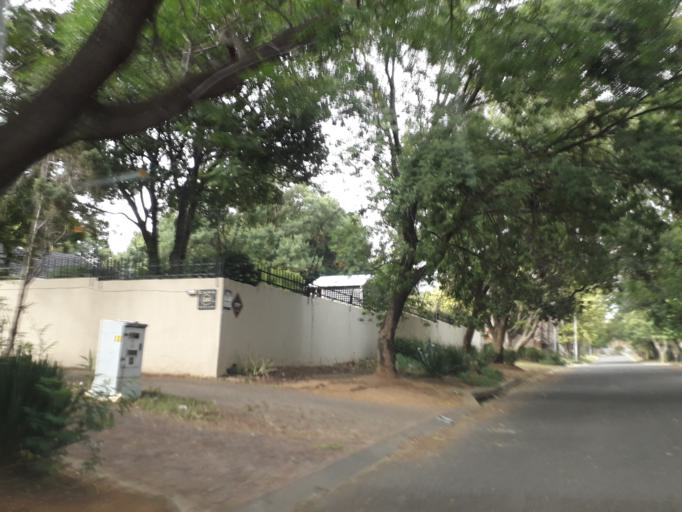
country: ZA
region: Gauteng
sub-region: City of Johannesburg Metropolitan Municipality
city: Roodepoort
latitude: -26.1044
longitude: 27.9585
